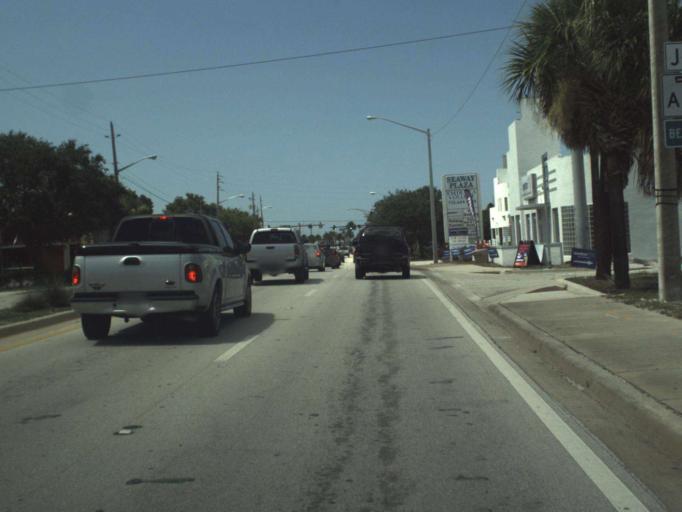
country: US
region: Florida
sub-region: Saint Lucie County
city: Fort Pierce
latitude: 27.4534
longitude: -80.3271
